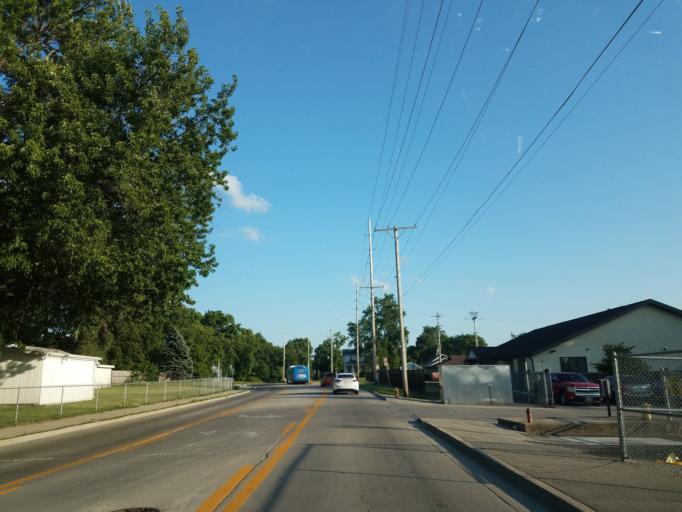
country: US
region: Illinois
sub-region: McLean County
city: Bloomington
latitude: 40.4773
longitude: -89.0164
